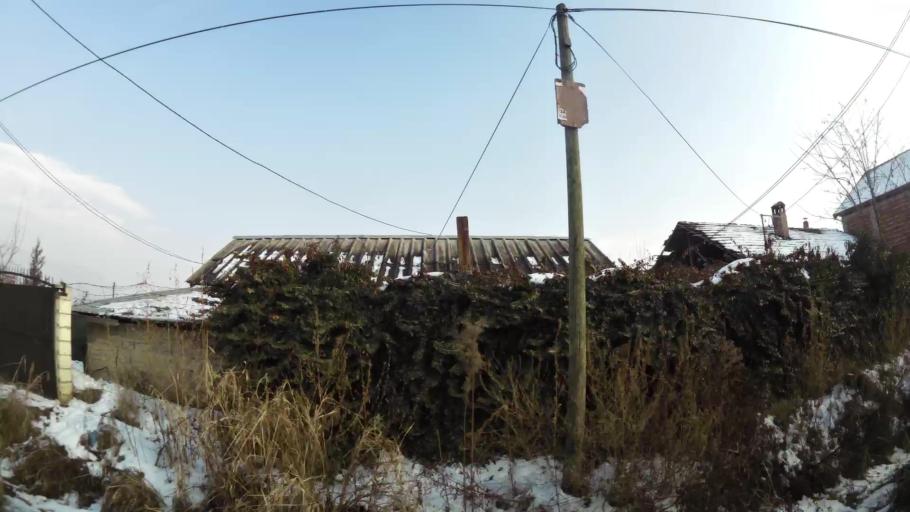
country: MK
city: Creshevo
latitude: 42.0230
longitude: 21.5103
